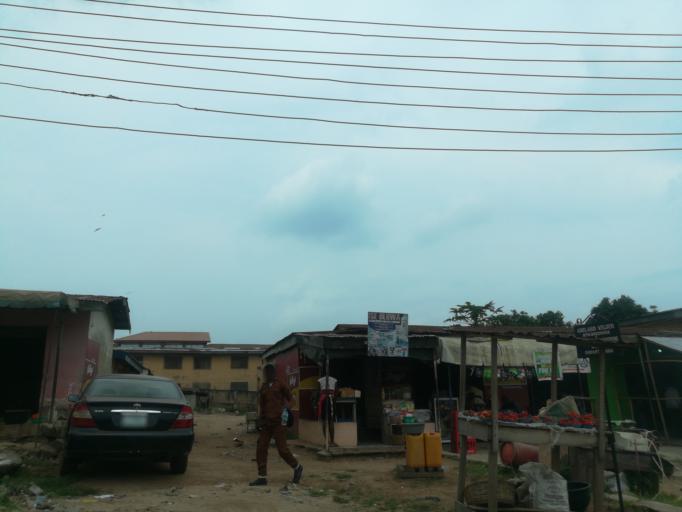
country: NG
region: Oyo
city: Ibadan
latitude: 7.4281
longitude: 3.9248
